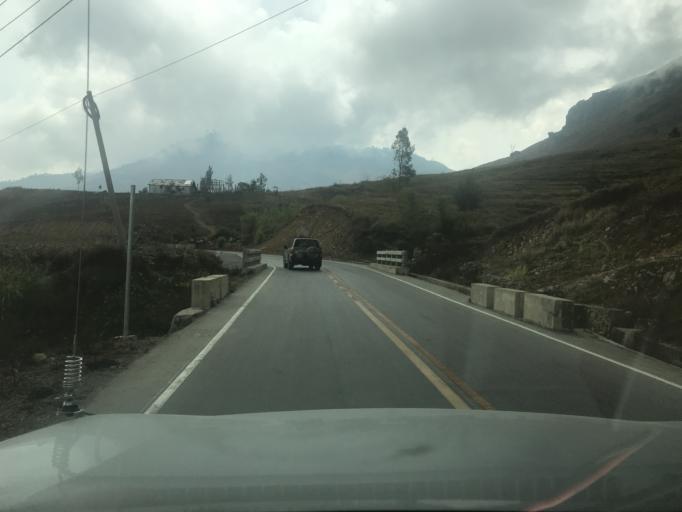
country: TL
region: Manufahi
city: Same
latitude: -8.8907
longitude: 125.5976
